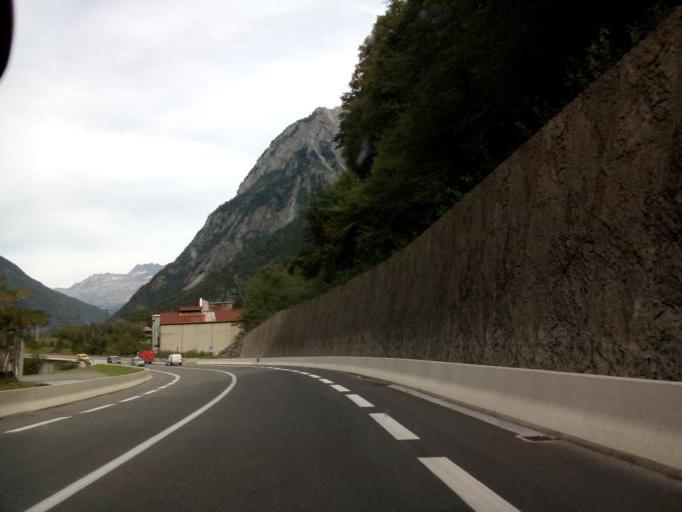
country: FR
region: Rhone-Alpes
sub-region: Departement de l'Isere
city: Livet-et-Gavet
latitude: 45.1065
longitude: 5.9332
